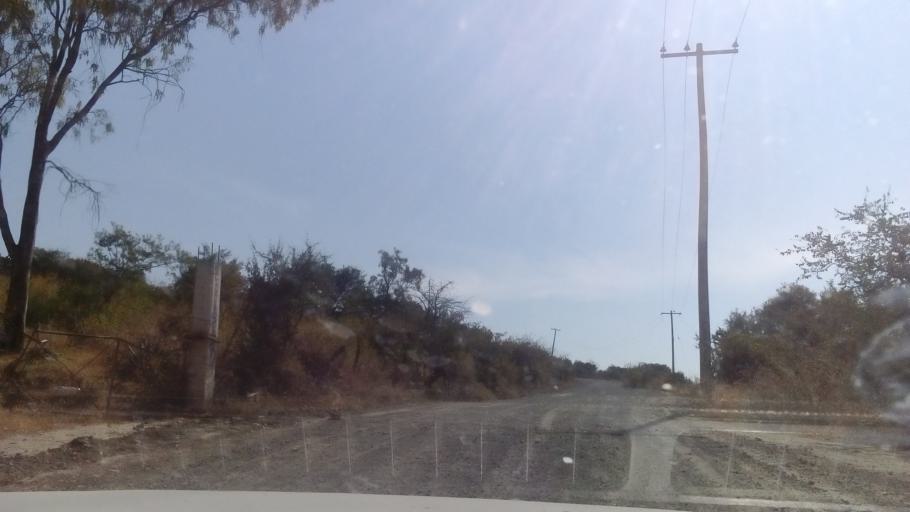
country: MX
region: Guanajuato
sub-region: Leon
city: Medina
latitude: 21.1439
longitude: -101.6052
